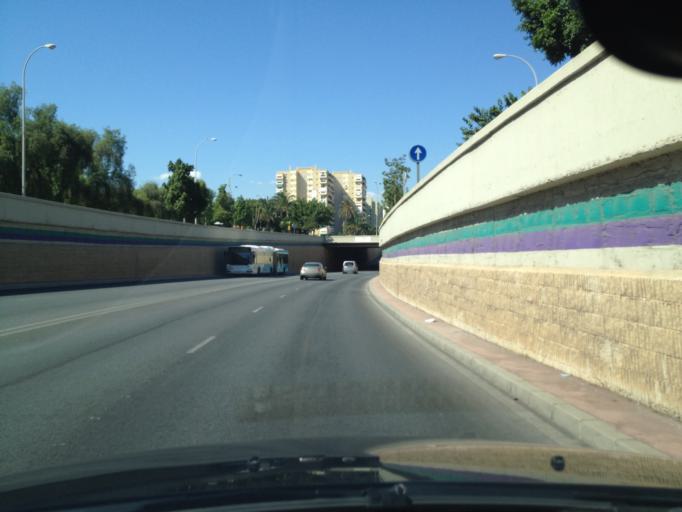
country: ES
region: Andalusia
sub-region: Provincia de Malaga
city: Malaga
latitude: 36.7136
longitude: -4.4475
